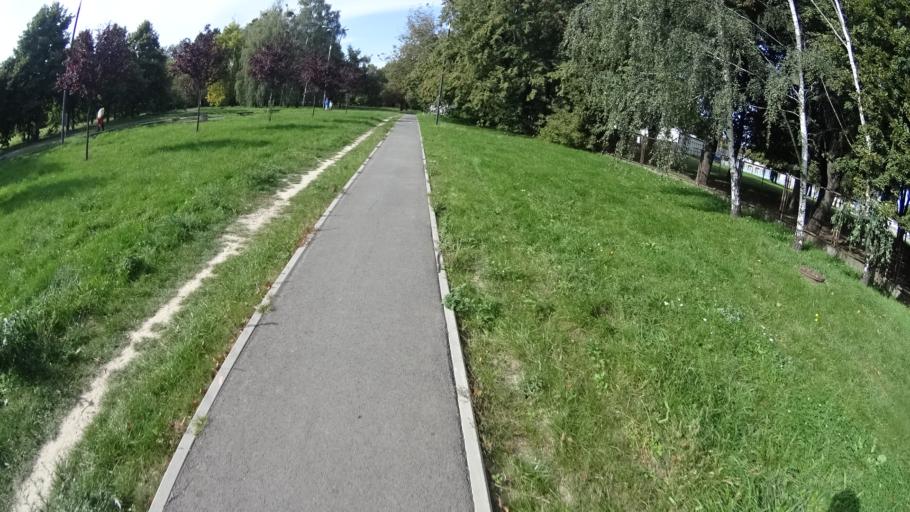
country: PL
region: Masovian Voivodeship
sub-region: Warszawa
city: Ochota
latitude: 52.2350
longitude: 20.9527
